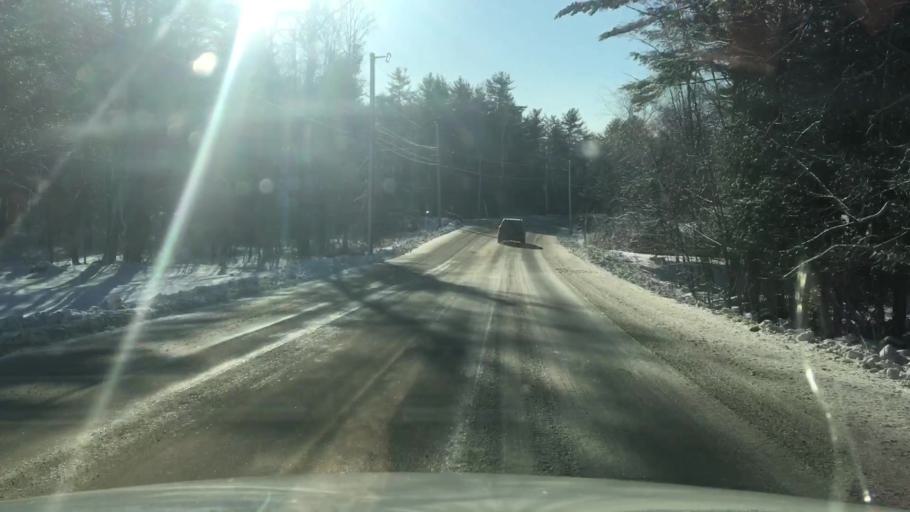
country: US
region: Maine
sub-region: Kennebec County
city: Readfield
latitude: 44.4035
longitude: -69.9637
